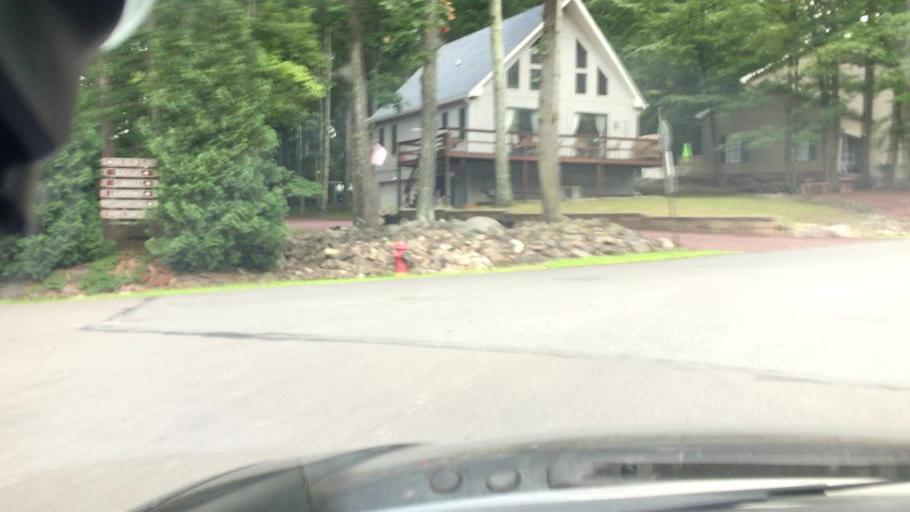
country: US
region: Pennsylvania
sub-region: Luzerne County
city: Freeland
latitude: 41.0427
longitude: -75.9336
